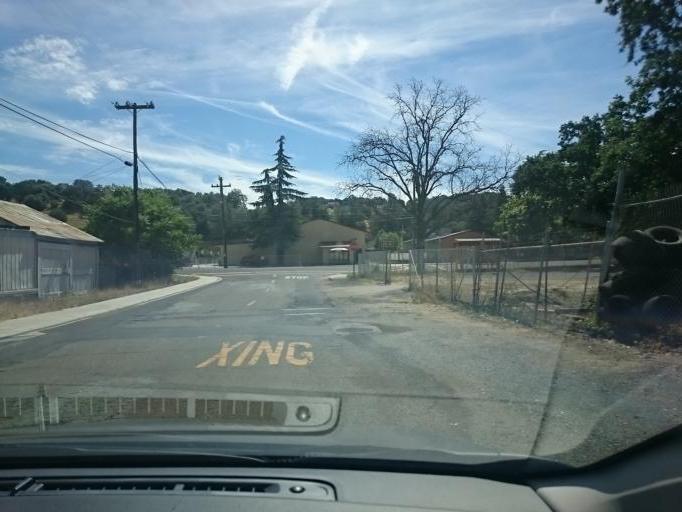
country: US
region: California
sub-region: Tuolumne County
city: Jamestown
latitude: 37.9545
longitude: -120.4188
